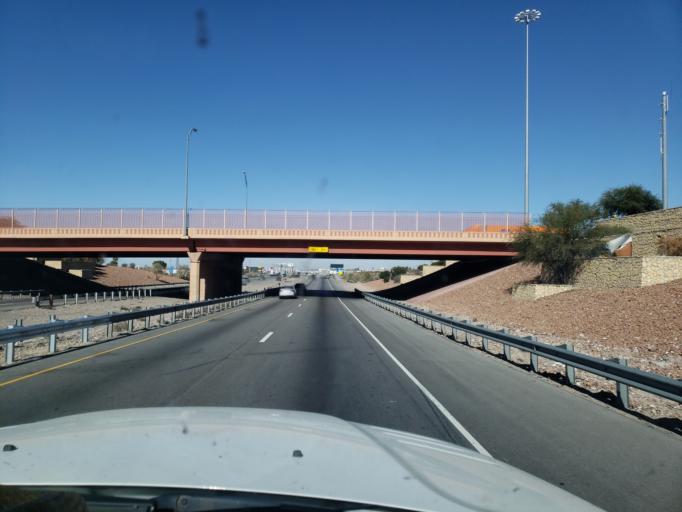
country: US
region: Texas
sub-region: El Paso County
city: Canutillo
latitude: 31.8825
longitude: -106.5817
